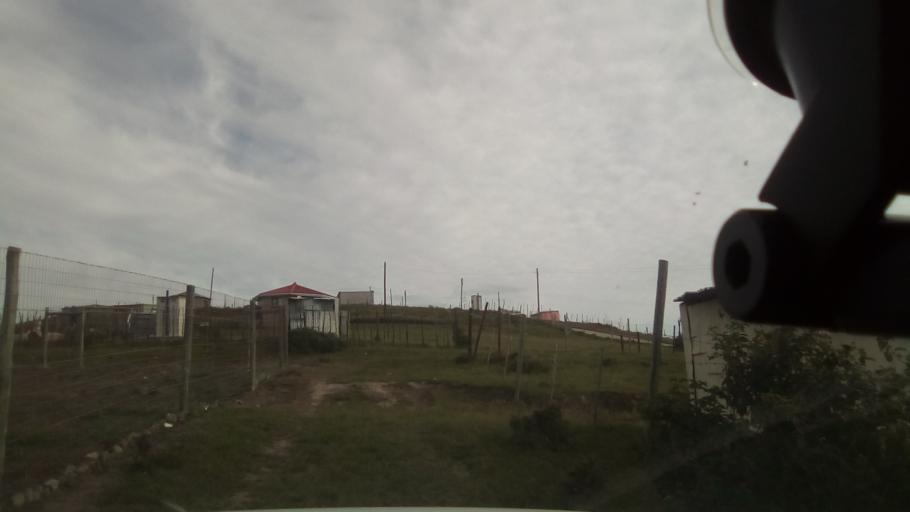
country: ZA
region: Eastern Cape
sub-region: Buffalo City Metropolitan Municipality
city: East London
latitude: -32.8006
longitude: 27.9665
